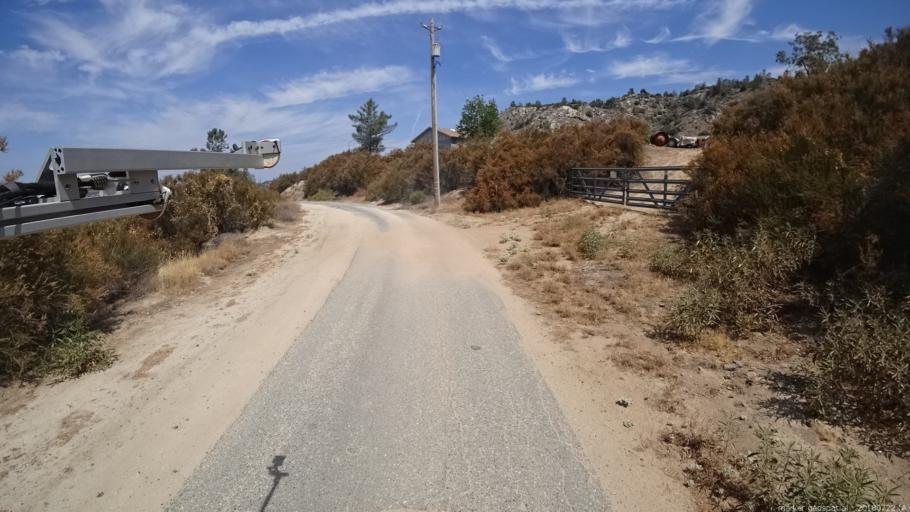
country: US
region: California
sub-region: Madera County
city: Coarsegold
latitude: 37.2599
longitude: -119.7508
